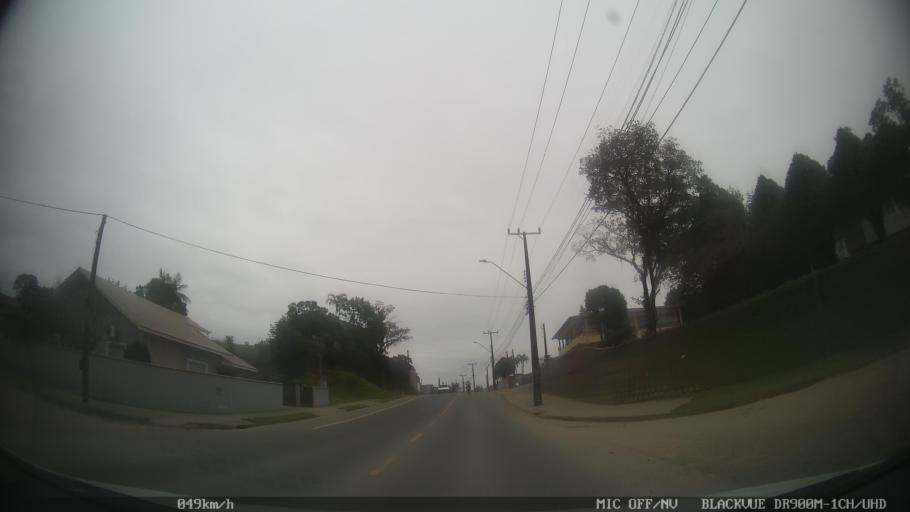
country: BR
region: Santa Catarina
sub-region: Joinville
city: Joinville
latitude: -26.3449
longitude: -48.8174
